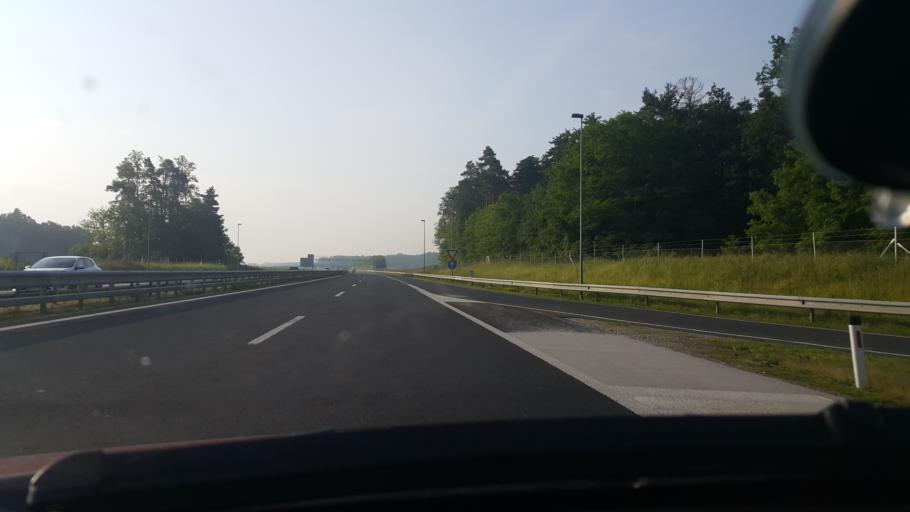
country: SI
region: Kidricevo
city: Kidricevo
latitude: 46.4112
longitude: 15.8119
